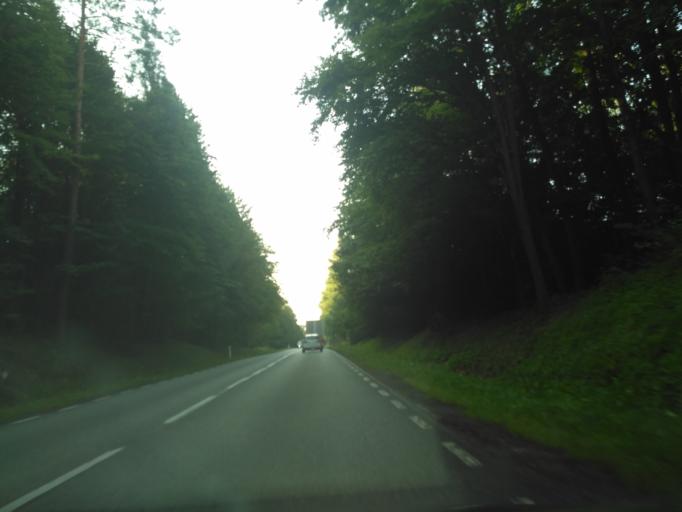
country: PL
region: Lublin Voivodeship
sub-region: Powiat krasnicki
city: Szastarka
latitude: 50.8506
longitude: 22.2889
